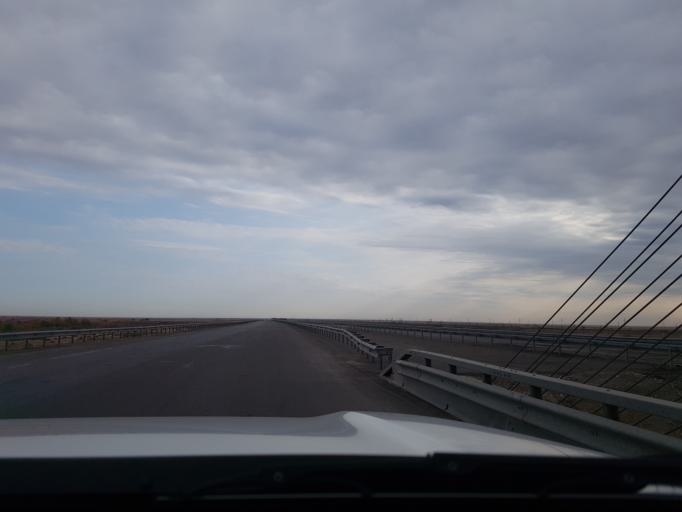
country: TM
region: Ahal
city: Tejen
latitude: 37.2325
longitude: 60.1521
